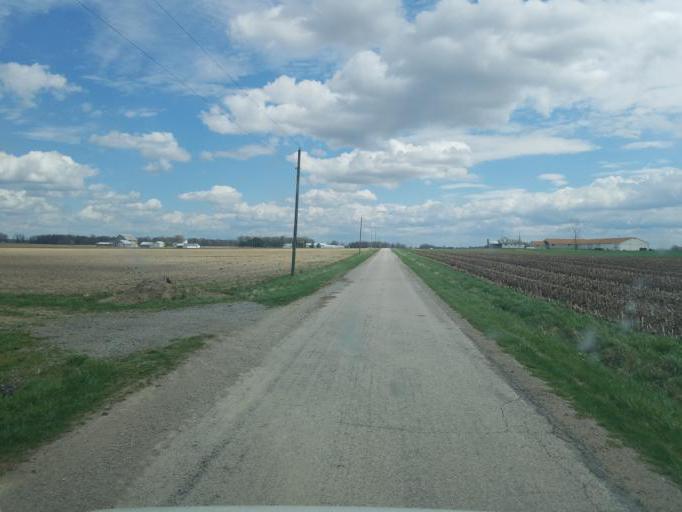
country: US
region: Ohio
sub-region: Crawford County
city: Bucyrus
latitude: 40.9216
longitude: -82.9088
